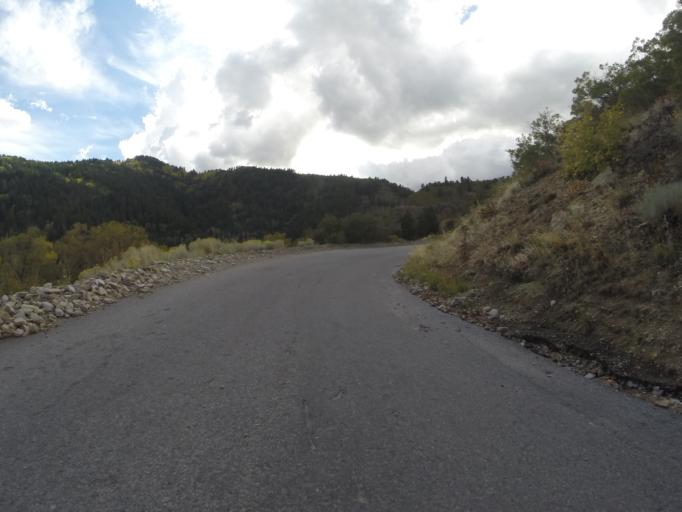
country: US
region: Utah
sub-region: Tooele County
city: Tooele
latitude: 40.4887
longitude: -112.1709
